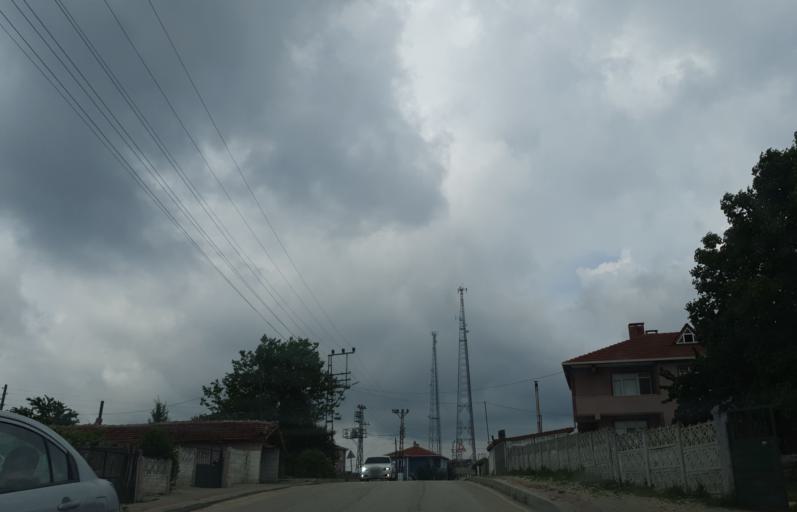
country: TR
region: Tekirdag
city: Saray
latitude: 41.4966
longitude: 27.9873
